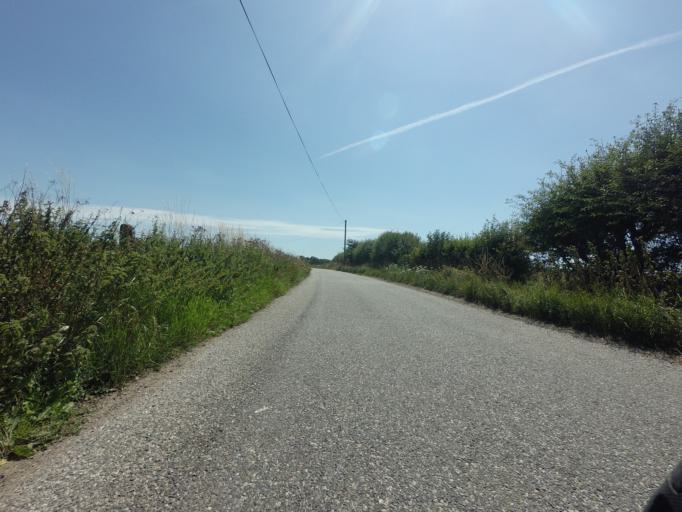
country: GB
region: England
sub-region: Kent
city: Lydd
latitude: 50.9635
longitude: 0.9010
